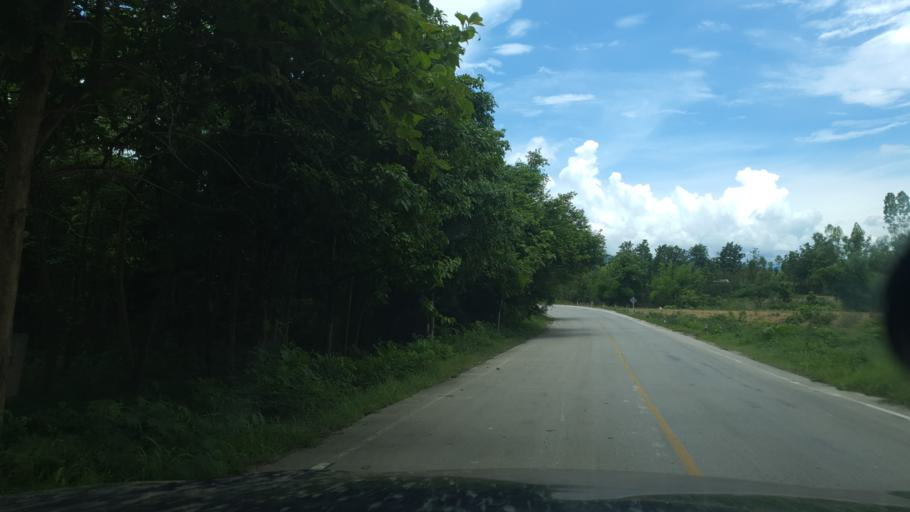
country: TH
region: Lampang
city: Sop Prap
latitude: 17.9164
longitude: 99.3879
